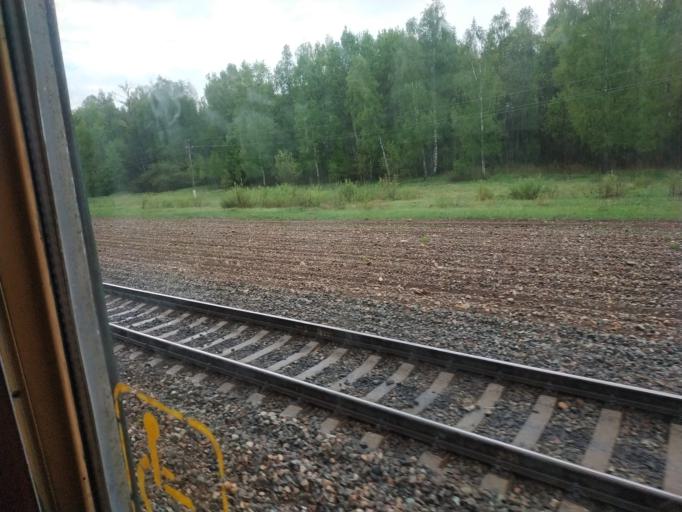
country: RU
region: Kaluga
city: Baryatino
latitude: 54.3530
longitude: 34.3227
